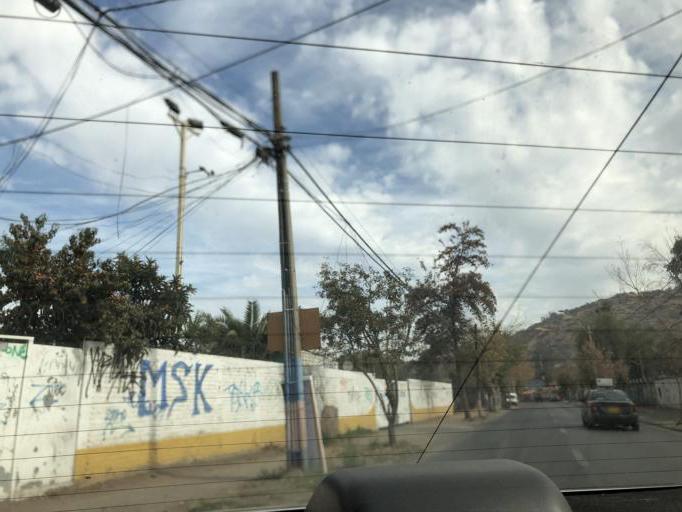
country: CL
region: Santiago Metropolitan
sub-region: Provincia de Cordillera
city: Puente Alto
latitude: -33.6084
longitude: -70.5369
